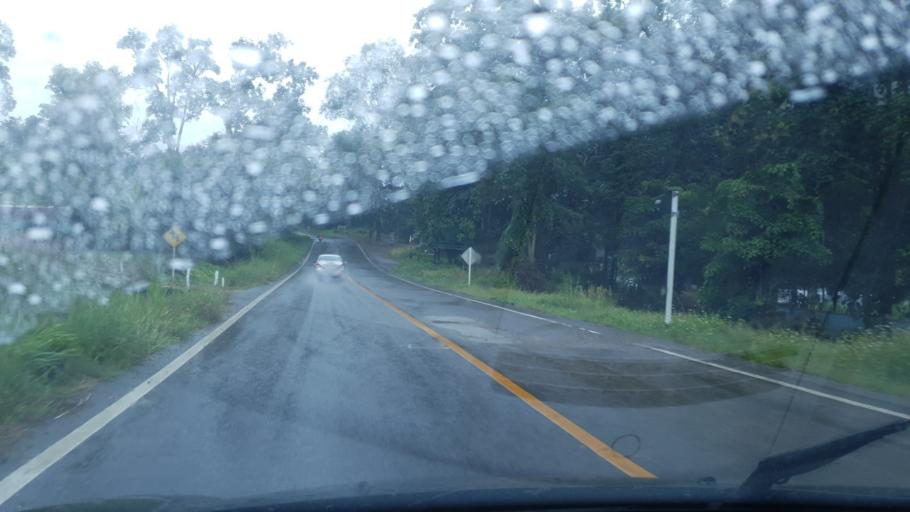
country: TH
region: Mae Hong Son
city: Khun Yuam
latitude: 18.6635
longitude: 97.9279
